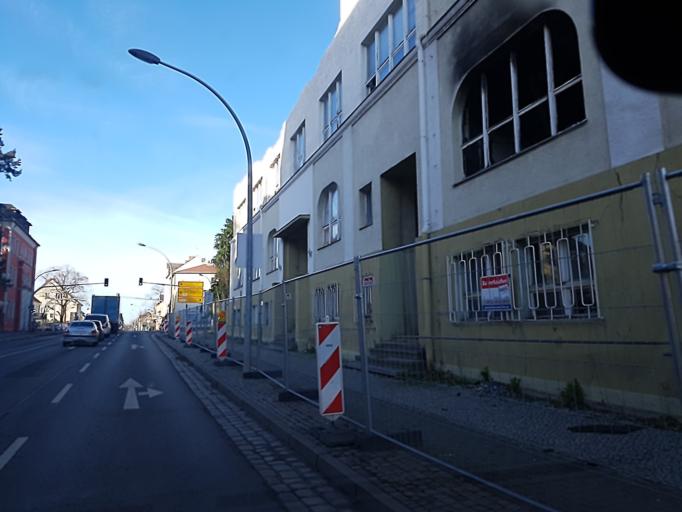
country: DE
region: Brandenburg
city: Finsterwalde
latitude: 51.6361
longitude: 13.7071
